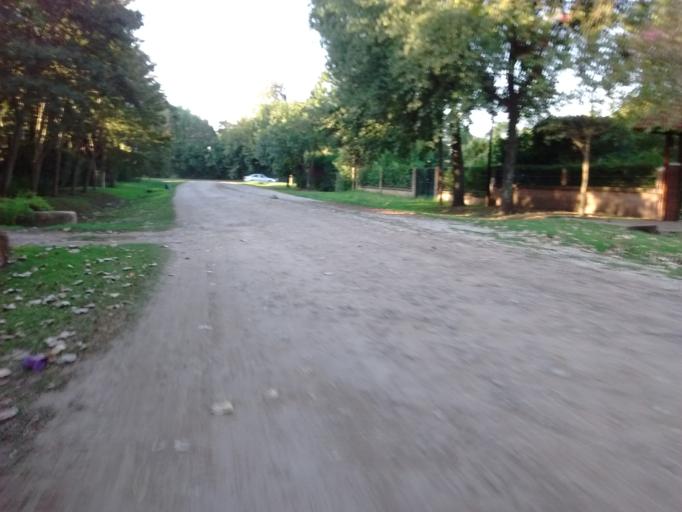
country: AR
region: Santa Fe
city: Funes
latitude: -32.9202
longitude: -60.8272
